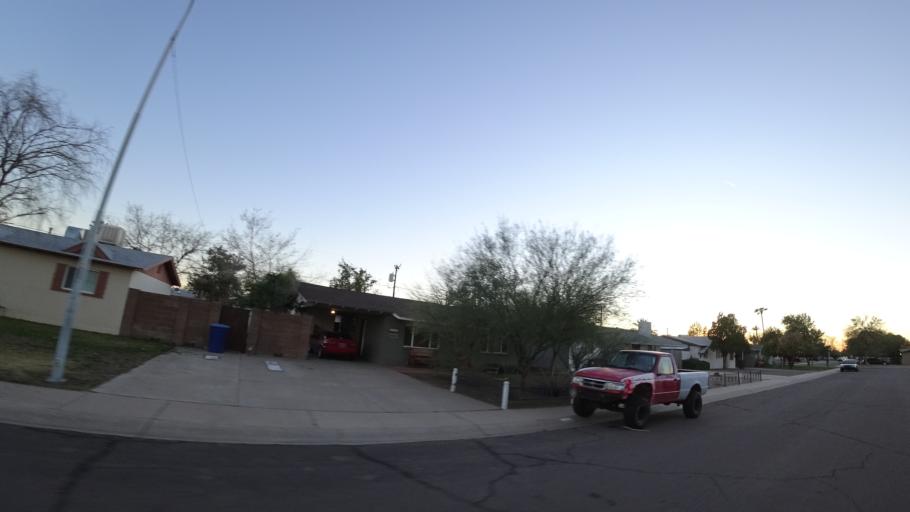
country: US
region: Arizona
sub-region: Maricopa County
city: Tempe Junction
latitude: 33.4197
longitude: -111.9555
